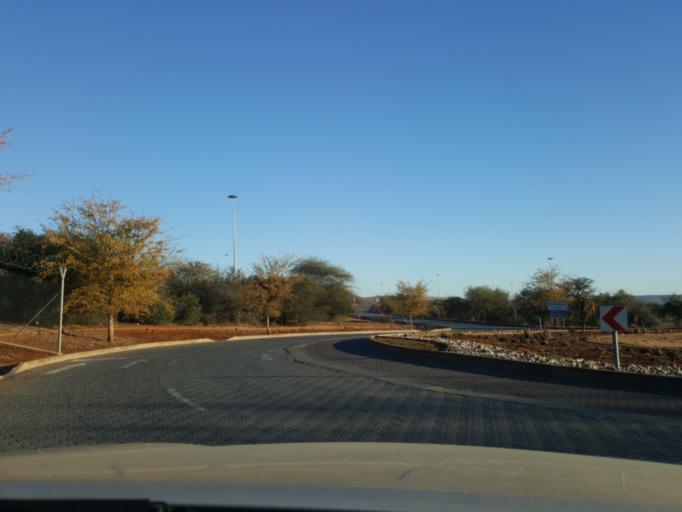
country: BW
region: South East
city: Lobatse
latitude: -25.2822
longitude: 25.7198
